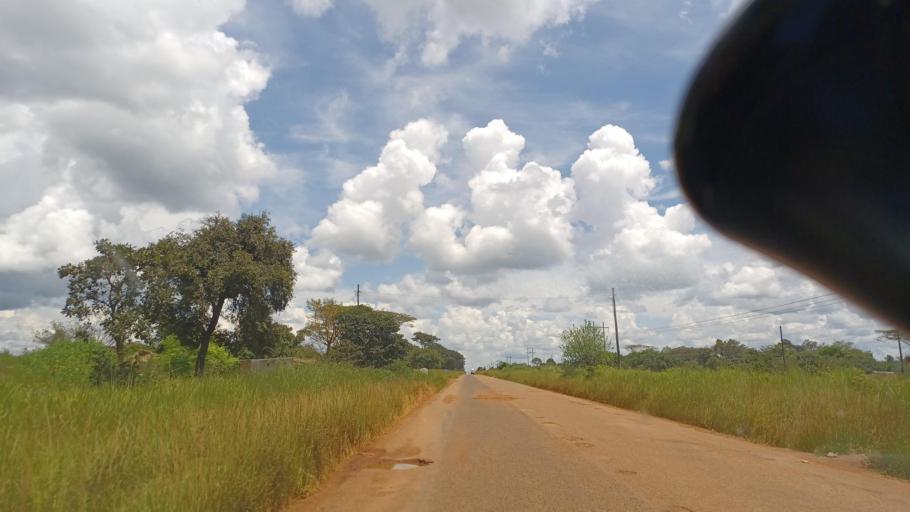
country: ZM
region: North-Western
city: Solwezi
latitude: -12.4874
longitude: 26.1930
